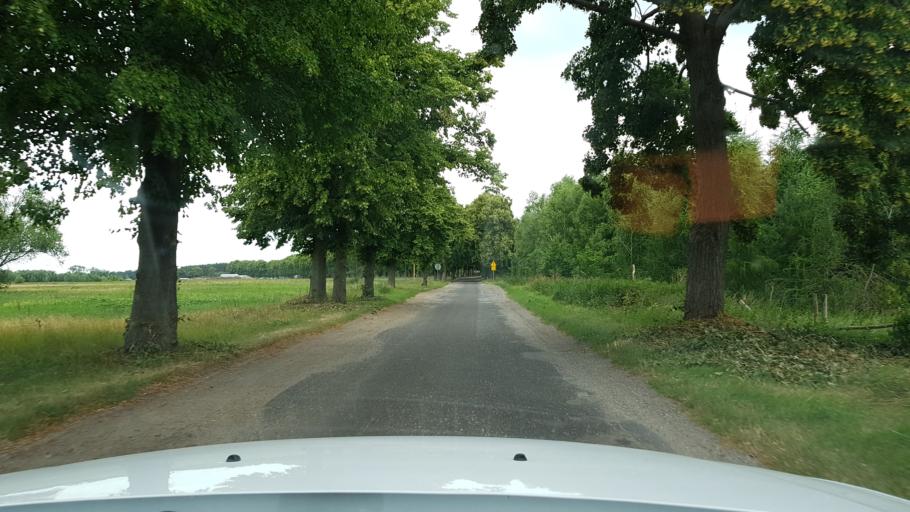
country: DE
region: Brandenburg
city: Manschnow
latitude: 52.6313
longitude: 14.5651
